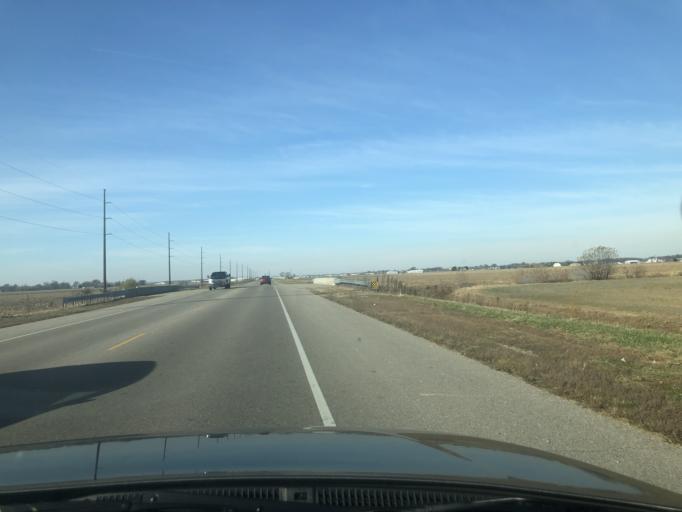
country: US
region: Indiana
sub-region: Warrick County
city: Newburgh
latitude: 37.9913
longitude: -87.4225
